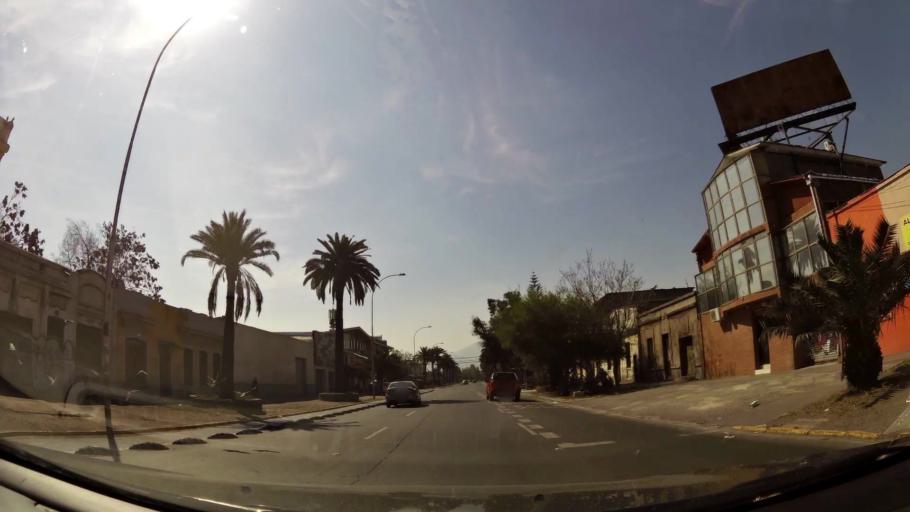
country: CL
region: Santiago Metropolitan
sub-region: Provincia de Santiago
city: Santiago
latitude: -33.4242
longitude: -70.6511
